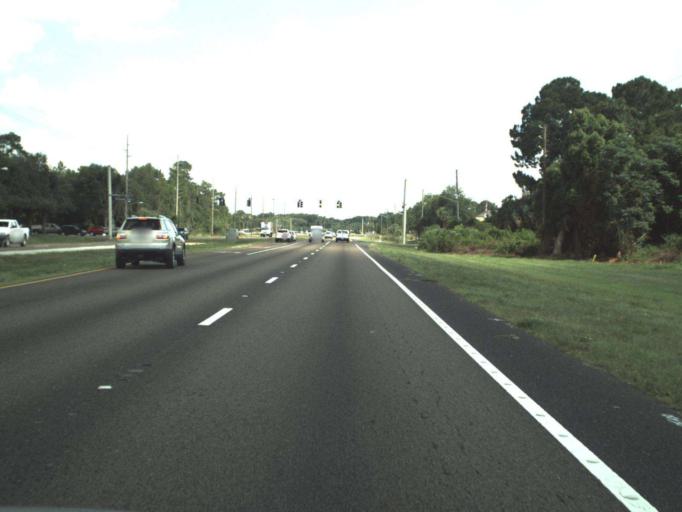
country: US
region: Florida
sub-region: Lake County
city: Mount Dora
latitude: 28.8198
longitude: -81.6333
